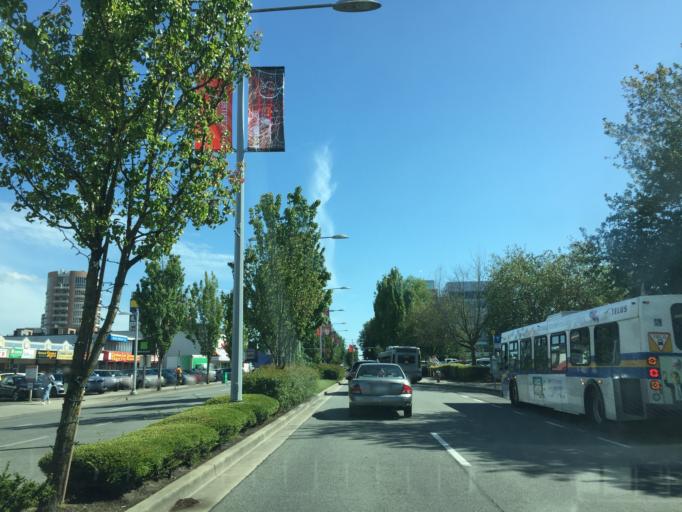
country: CA
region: British Columbia
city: Richmond
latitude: 49.1663
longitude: -123.1366
